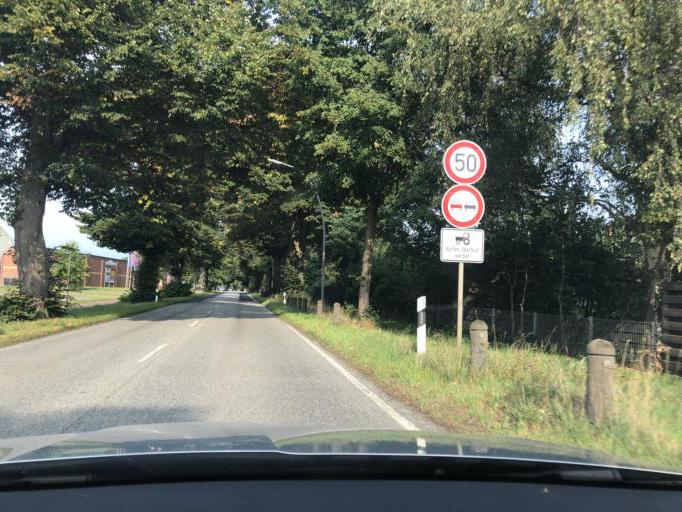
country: DE
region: Schleswig-Holstein
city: Gross Gronau
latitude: 53.8131
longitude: 10.7415
